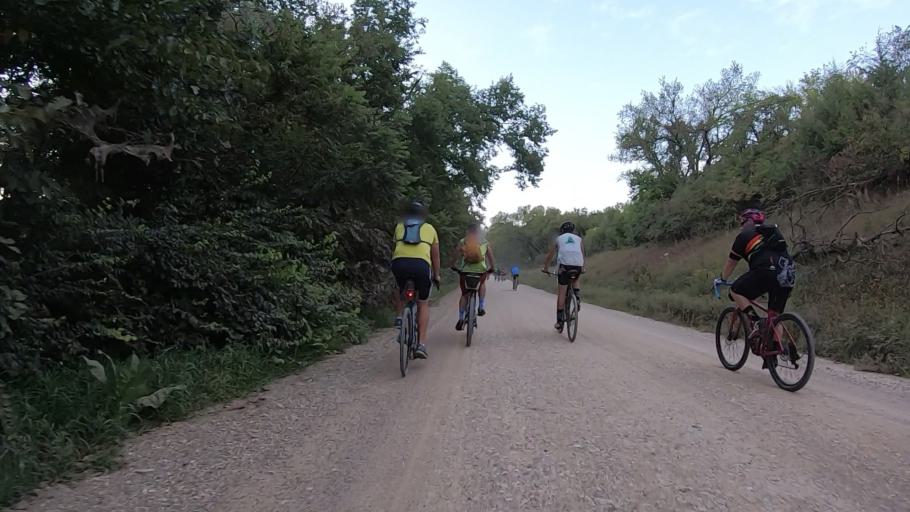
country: US
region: Kansas
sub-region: Marshall County
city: Marysville
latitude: 39.8333
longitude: -96.6651
